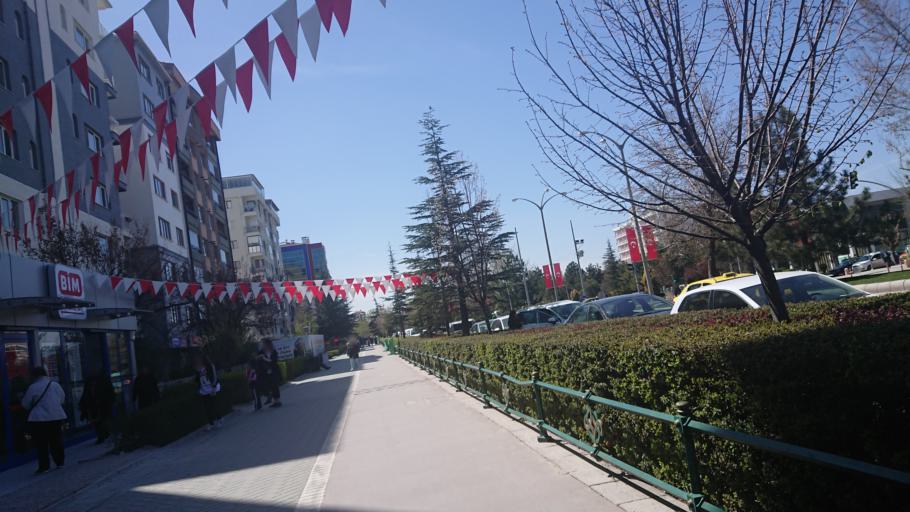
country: TR
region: Eskisehir
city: Eskisehir
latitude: 39.7649
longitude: 30.5144
